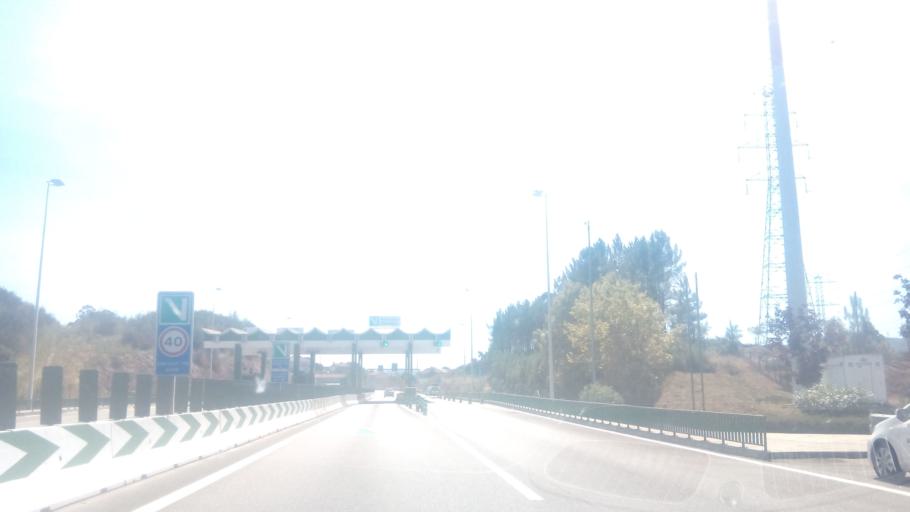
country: PT
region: Porto
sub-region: Valongo
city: Campo
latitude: 41.1845
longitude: -8.4549
